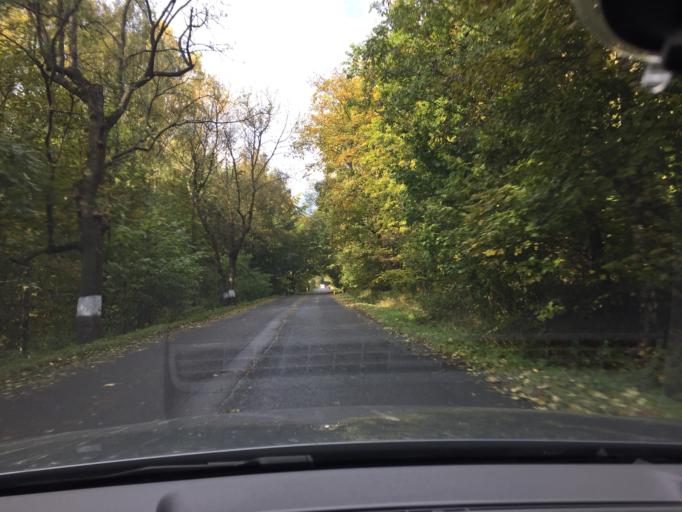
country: CZ
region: Ustecky
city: Chlumec
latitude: 50.7378
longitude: 13.9851
